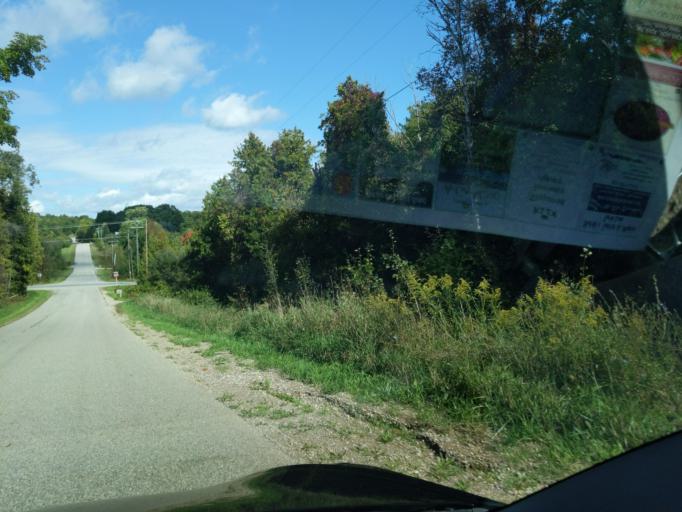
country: US
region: Michigan
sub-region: Antrim County
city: Elk Rapids
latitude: 44.9597
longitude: -85.3323
